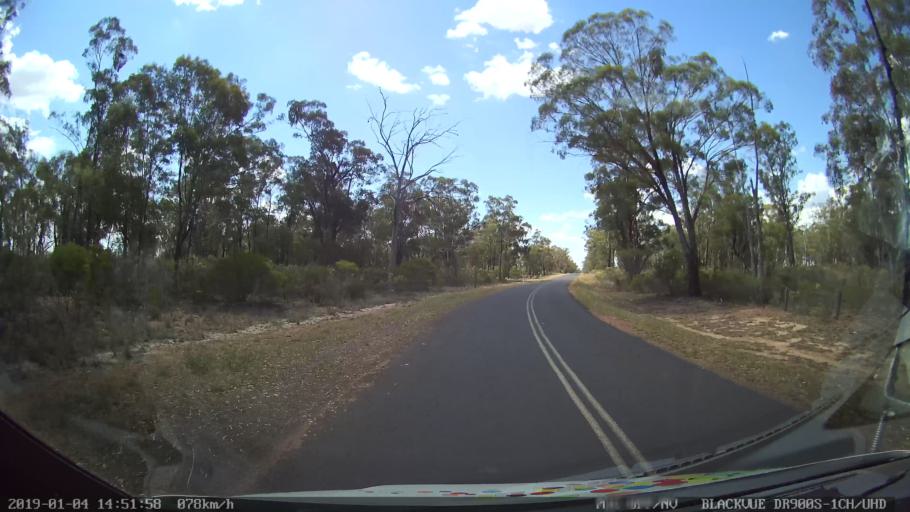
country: AU
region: New South Wales
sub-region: Dubbo Municipality
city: Dubbo
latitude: -32.0213
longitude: 148.6491
